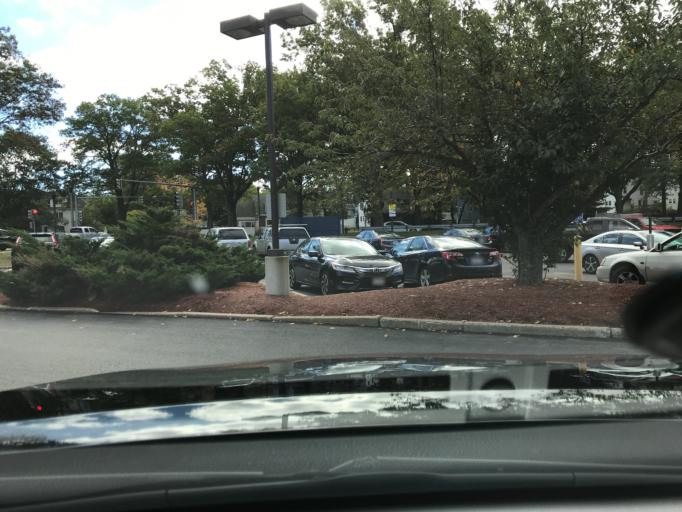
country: US
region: Massachusetts
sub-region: Suffolk County
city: Jamaica Plain
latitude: 42.2961
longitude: -71.1583
